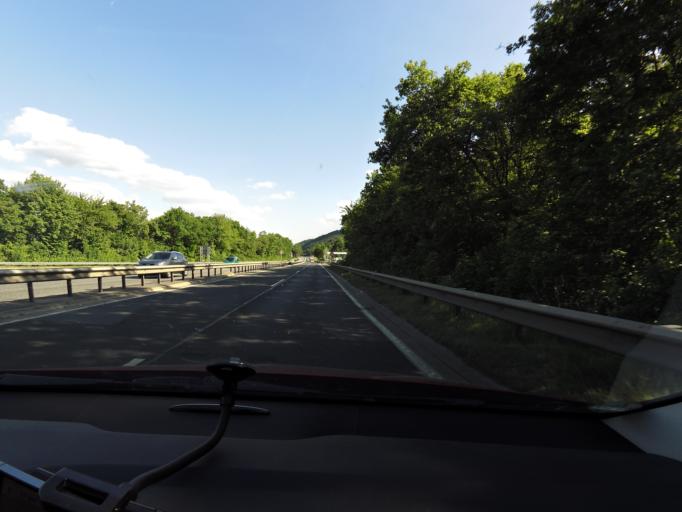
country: DE
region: Rheinland-Pfalz
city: Sinzig
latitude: 50.5420
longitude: 7.2611
